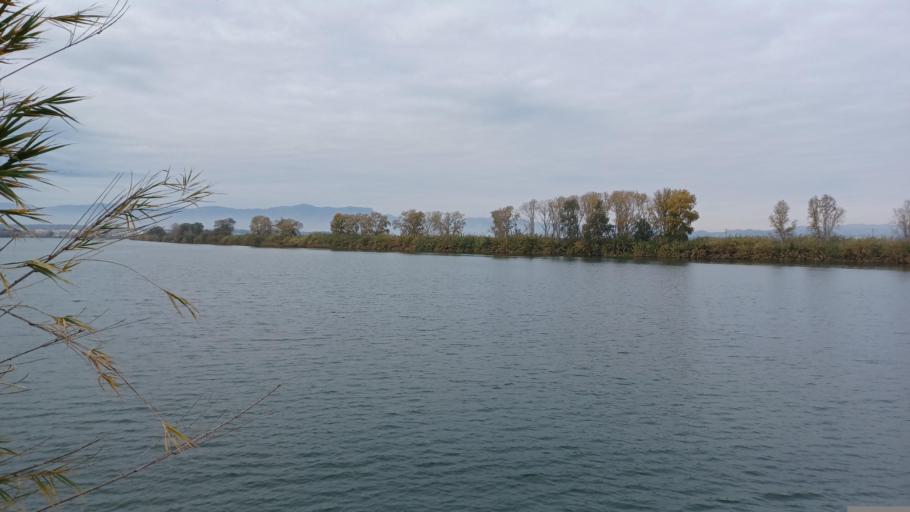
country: ES
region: Catalonia
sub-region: Provincia de Tarragona
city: Amposta
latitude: 40.7055
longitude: 0.6204
